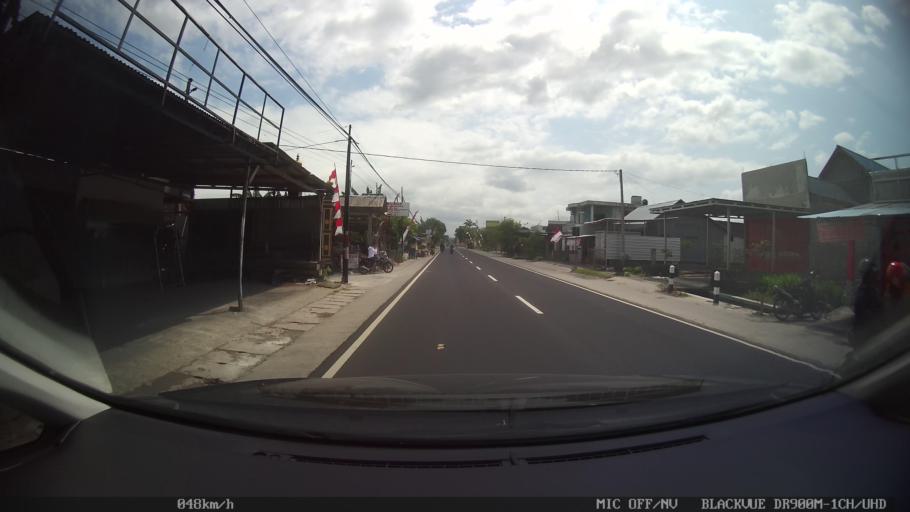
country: ID
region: Central Java
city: Candi Prambanan
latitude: -7.8190
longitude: 110.4809
